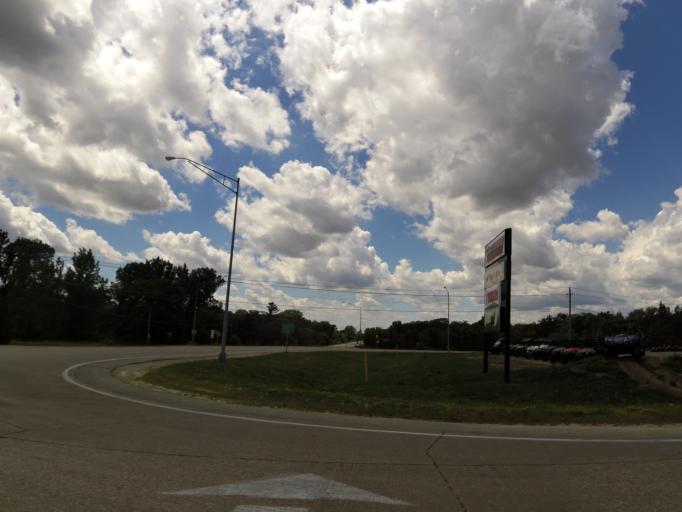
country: US
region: Iowa
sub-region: Fayette County
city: Oelwein
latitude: 42.6426
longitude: -91.9088
